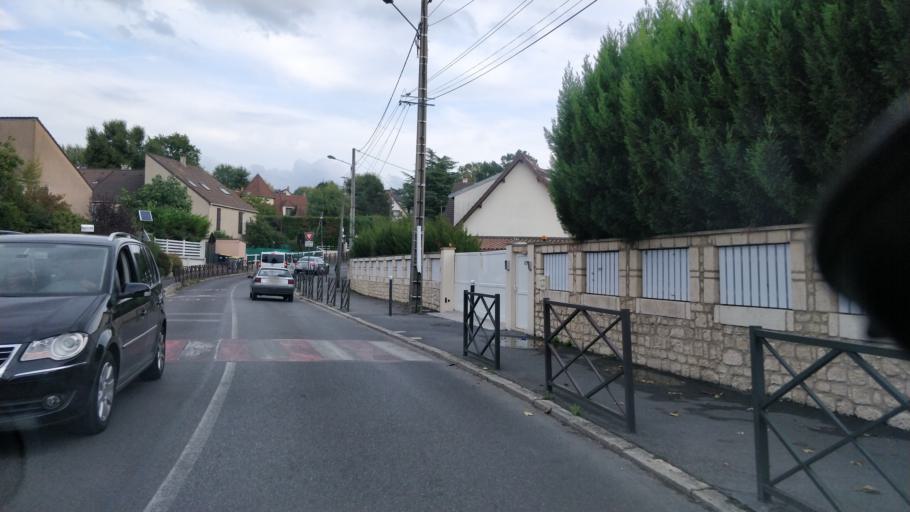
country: FR
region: Ile-de-France
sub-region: Departement de Seine-Saint-Denis
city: Livry-Gargan
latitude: 48.9167
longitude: 2.5465
